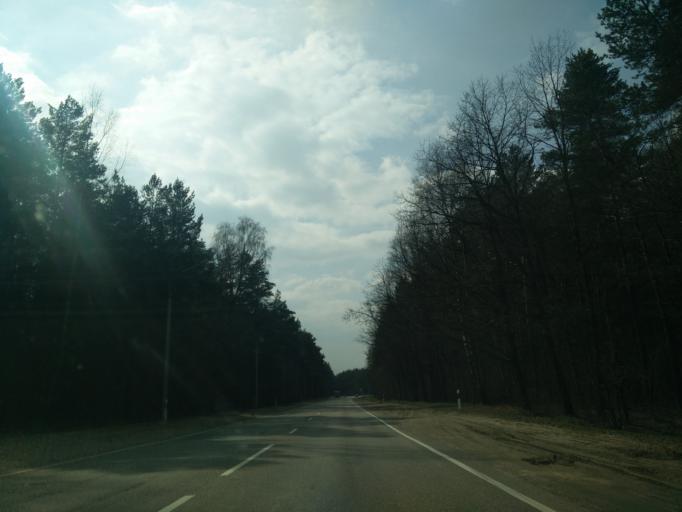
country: LT
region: Vilnius County
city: Lazdynai
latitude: 54.6379
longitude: 25.1765
